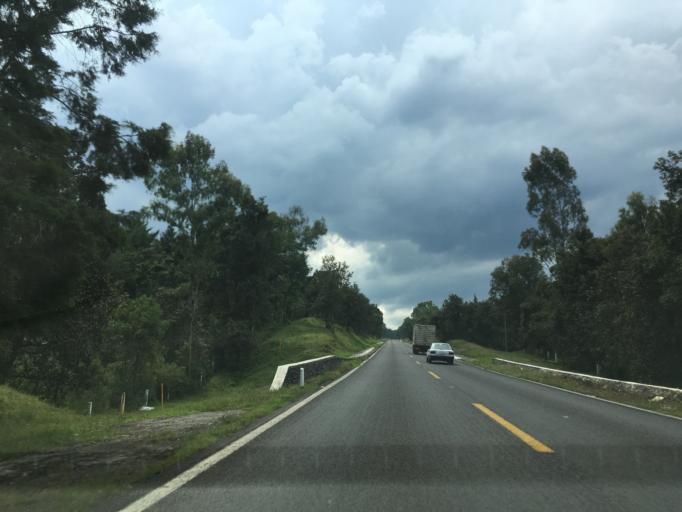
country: MX
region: Michoacan
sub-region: Patzcuaro
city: Santa Ana Chapitiro
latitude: 19.5102
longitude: -101.6795
